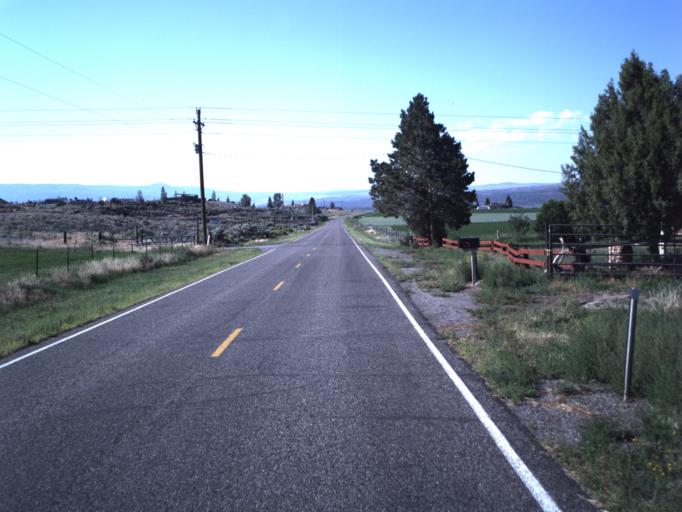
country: US
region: Utah
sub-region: Wayne County
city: Loa
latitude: 38.4195
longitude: -111.6202
